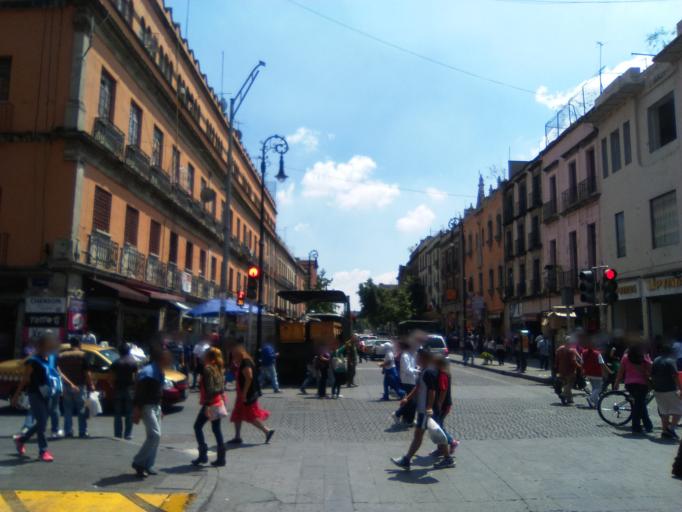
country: MX
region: Mexico City
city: Mexico City
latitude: 19.4315
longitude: -99.1303
